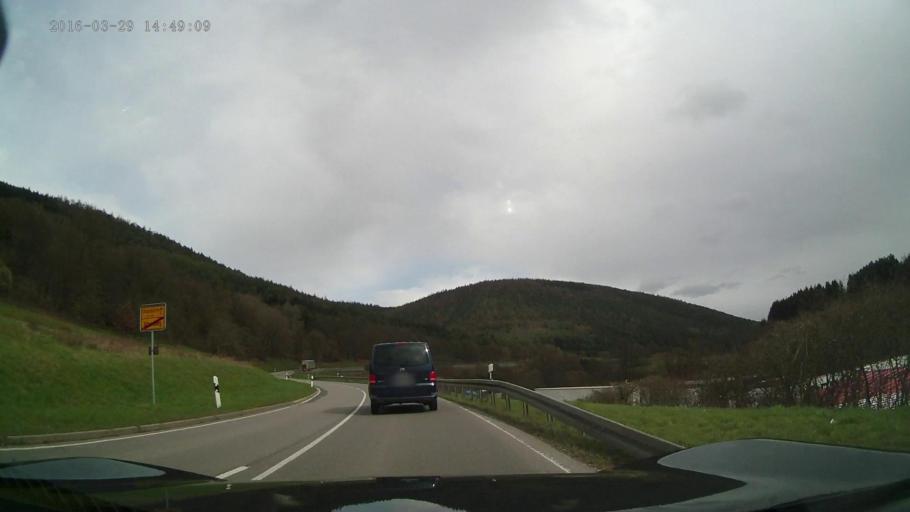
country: DE
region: Bavaria
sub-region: Regierungsbezirk Unterfranken
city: Weilbach
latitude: 49.6404
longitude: 9.2586
